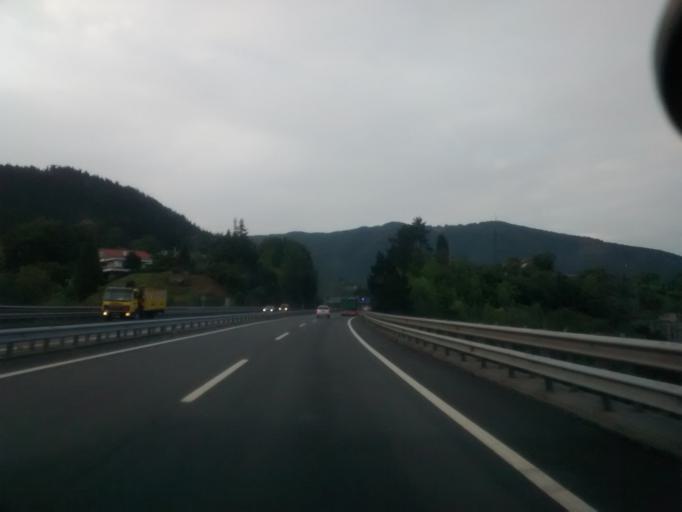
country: ES
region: Basque Country
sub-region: Provincia de Guipuzcoa
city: Elgoibar
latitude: 43.2282
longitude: -2.4031
